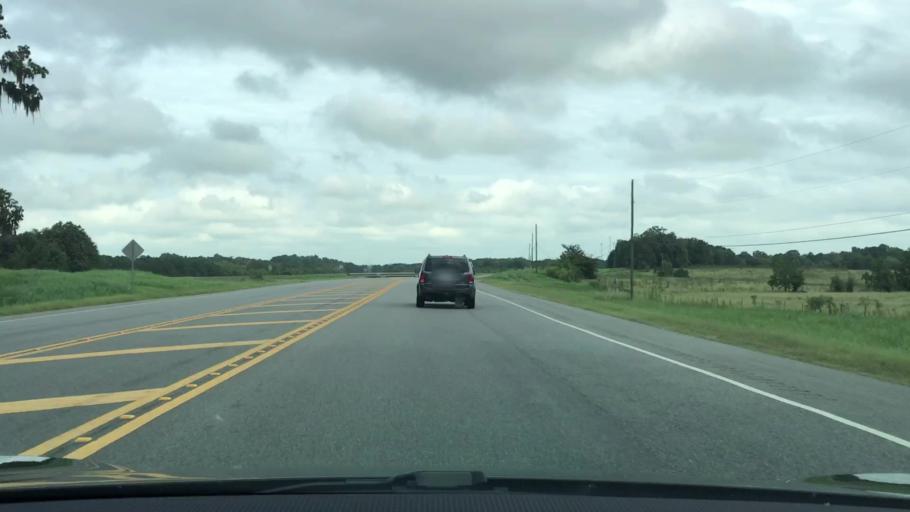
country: US
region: Alabama
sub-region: Montgomery County
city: Pike Road
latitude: 32.3332
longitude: -86.0578
